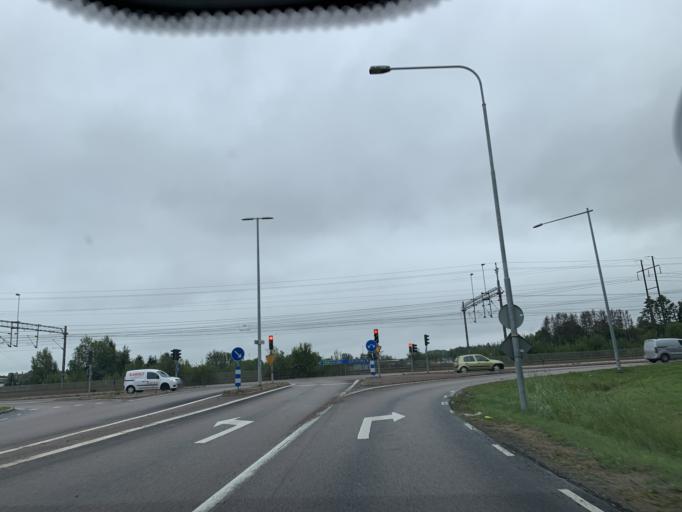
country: SE
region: Vaestmanland
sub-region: Vasteras
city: Vasteras
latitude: 59.5937
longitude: 16.4904
